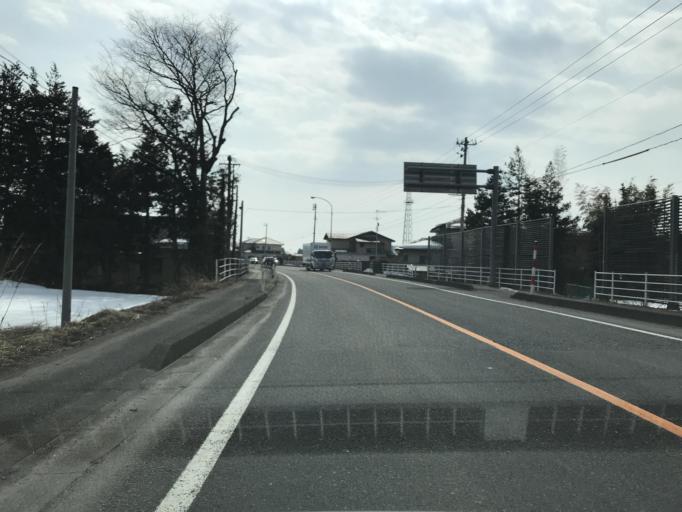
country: JP
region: Miyagi
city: Furukawa
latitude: 38.6937
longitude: 140.8462
